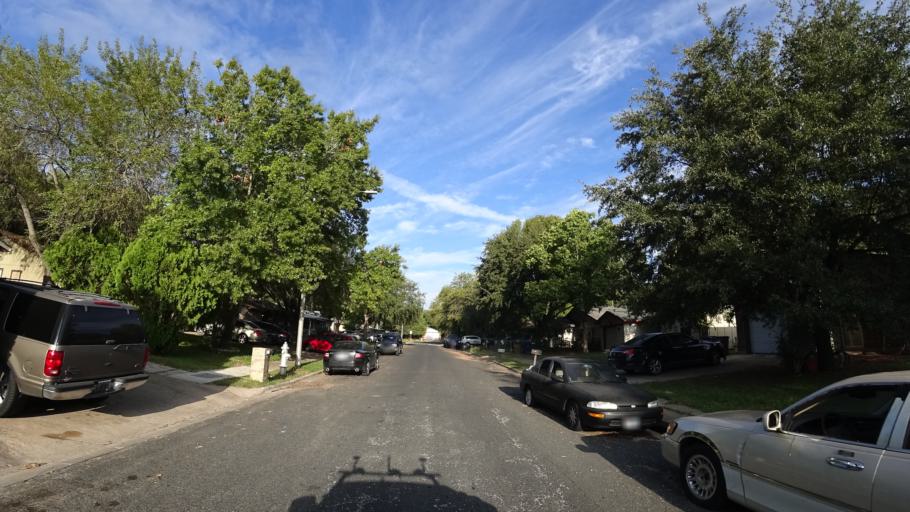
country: US
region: Texas
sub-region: Travis County
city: Onion Creek
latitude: 30.1895
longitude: -97.7477
